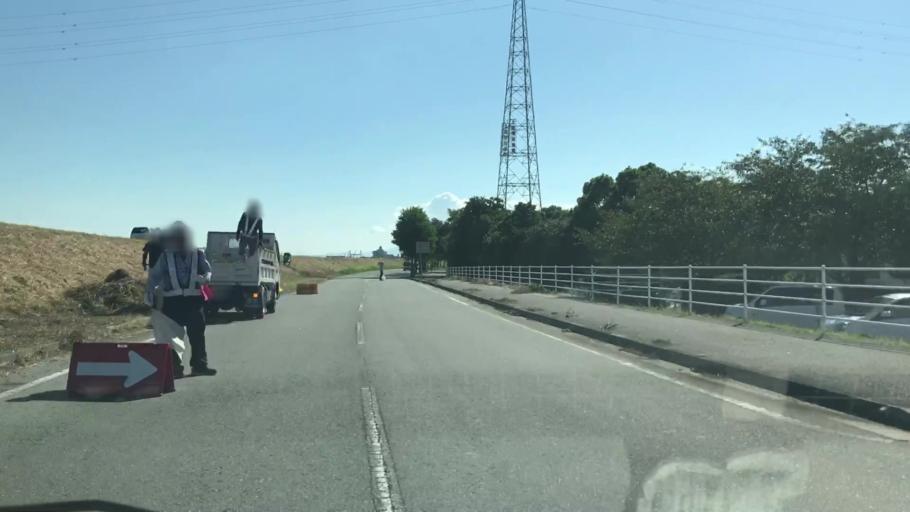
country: JP
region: Saga Prefecture
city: Okawa
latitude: 33.2315
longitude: 130.3775
